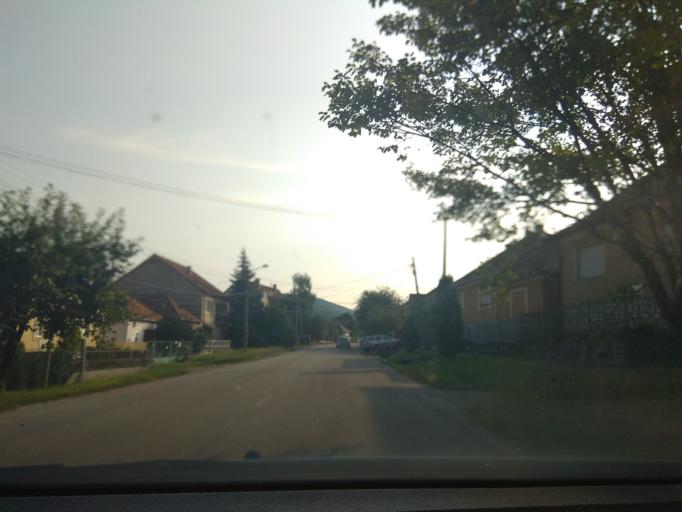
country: HU
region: Heves
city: Felsotarkany
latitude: 47.9766
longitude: 20.4218
